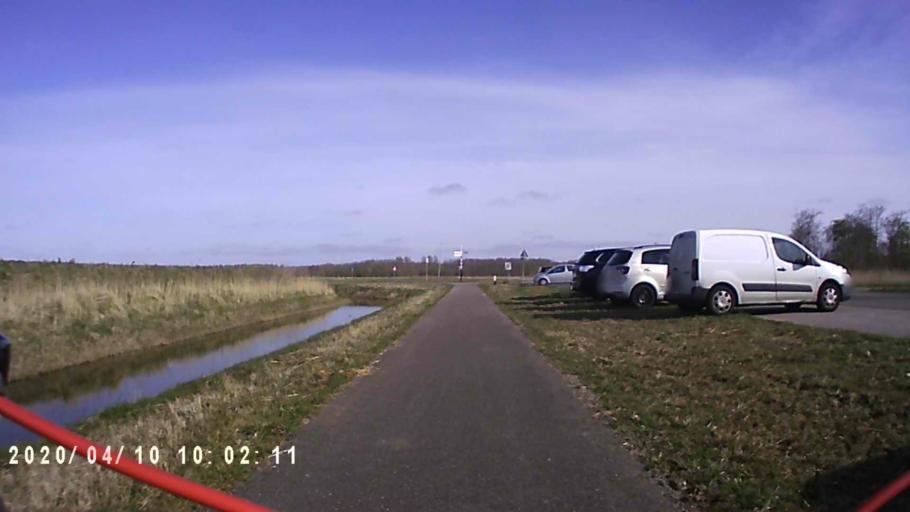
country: NL
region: Groningen
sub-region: Gemeente De Marne
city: Ulrum
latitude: 53.3639
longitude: 6.2604
